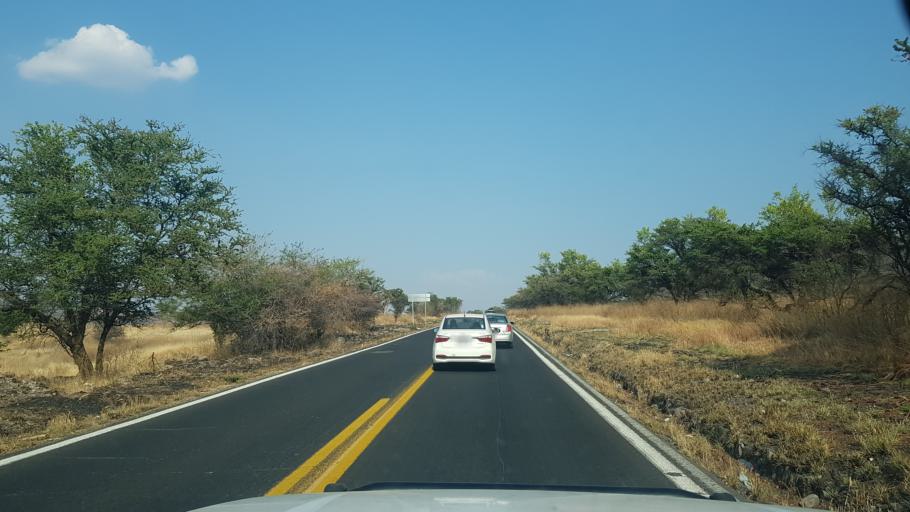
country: MX
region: Puebla
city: Calmeca
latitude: 18.6547
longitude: -98.6570
